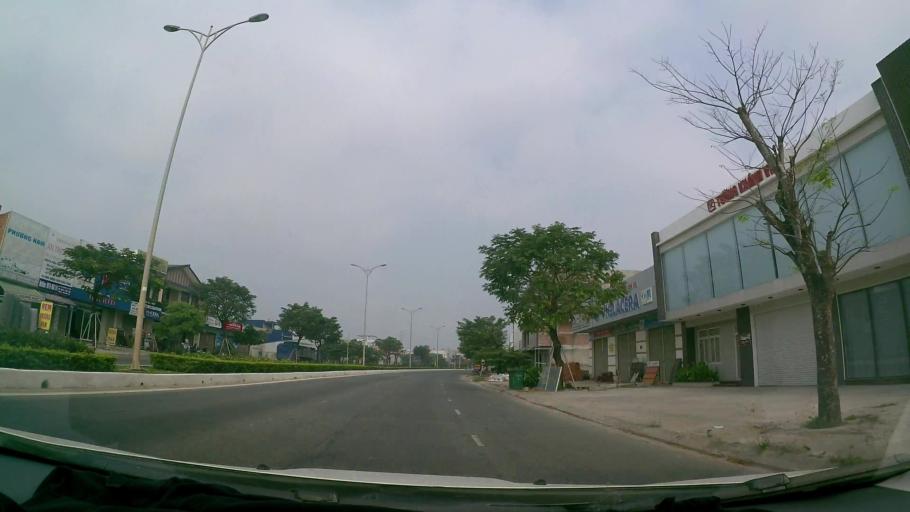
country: VN
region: Da Nang
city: Cam Le
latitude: 16.0049
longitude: 108.2225
